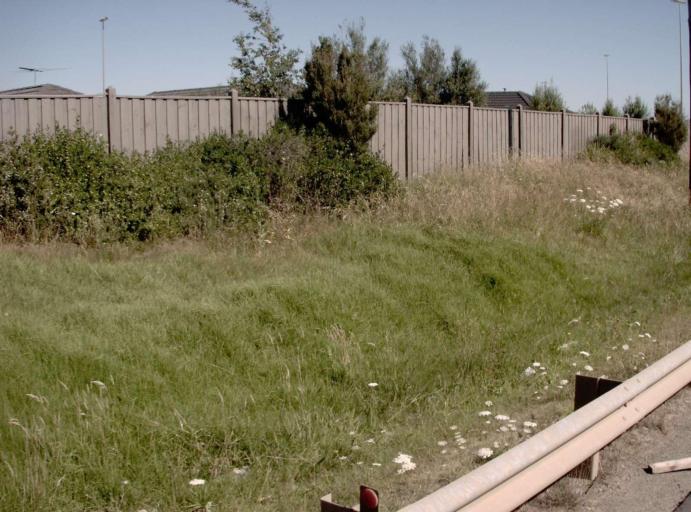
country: AU
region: Victoria
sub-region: Cardinia
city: Officer
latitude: -38.0658
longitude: 145.4369
